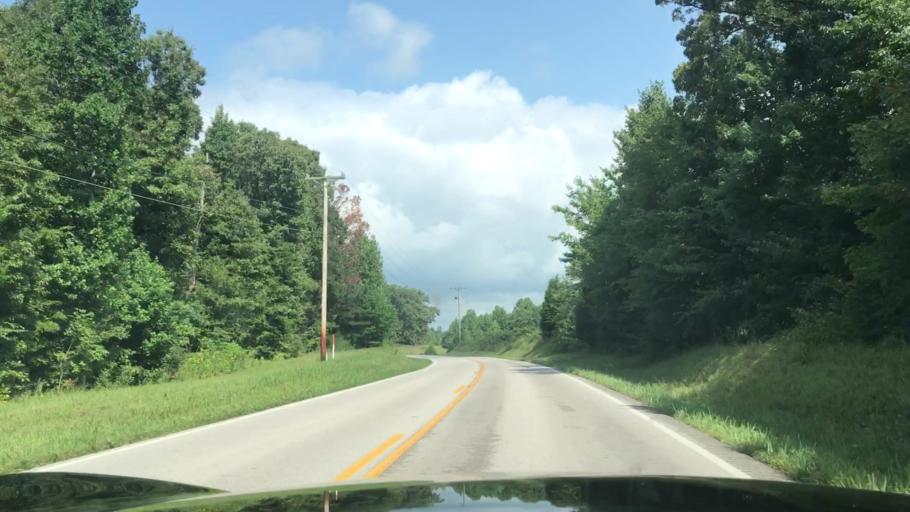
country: US
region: Kentucky
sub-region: Butler County
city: Morgantown
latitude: 37.1886
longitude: -86.8788
